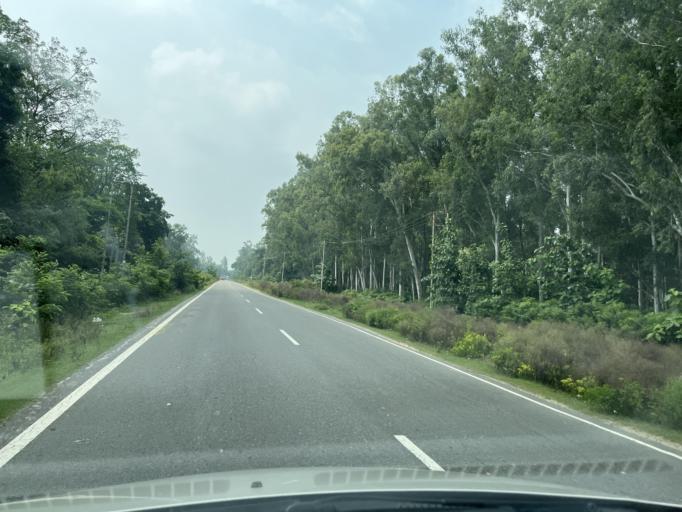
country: IN
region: Uttarakhand
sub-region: Haridwar
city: Sultanpur
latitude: 29.7546
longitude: 78.2657
